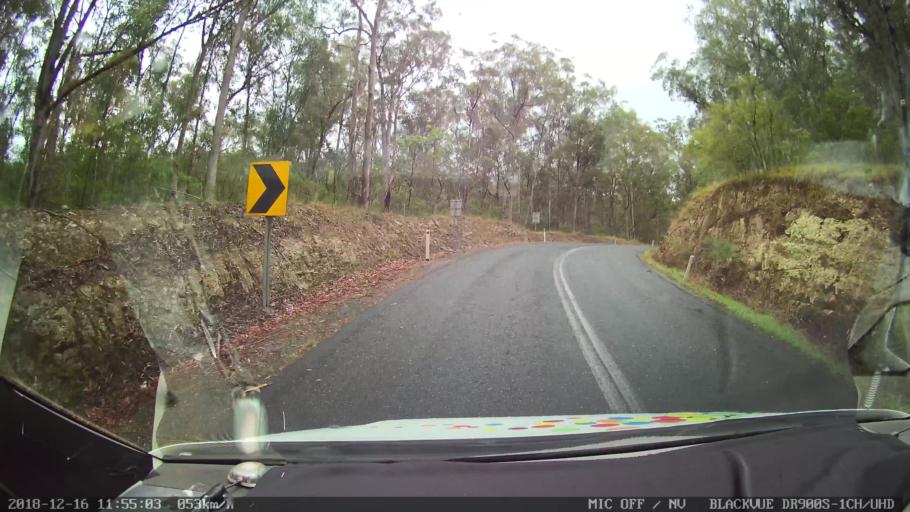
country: AU
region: New South Wales
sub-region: Tenterfield Municipality
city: Carrolls Creek
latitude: -28.9113
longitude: 152.2888
